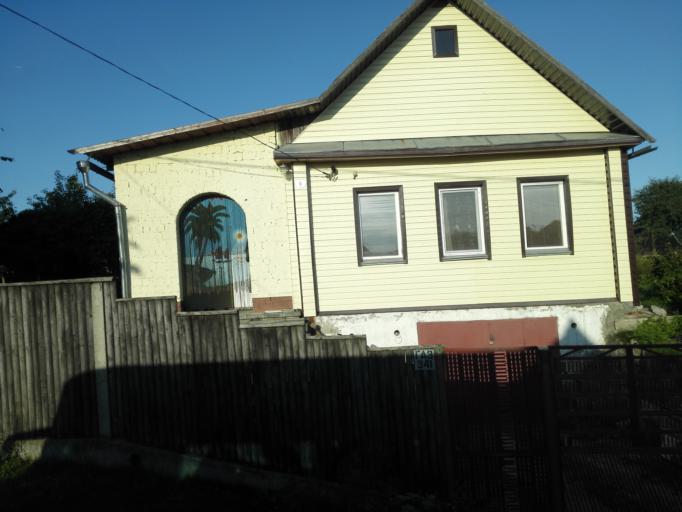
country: BY
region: Mogilev
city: Yalizava
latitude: 53.3265
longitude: 29.0499
